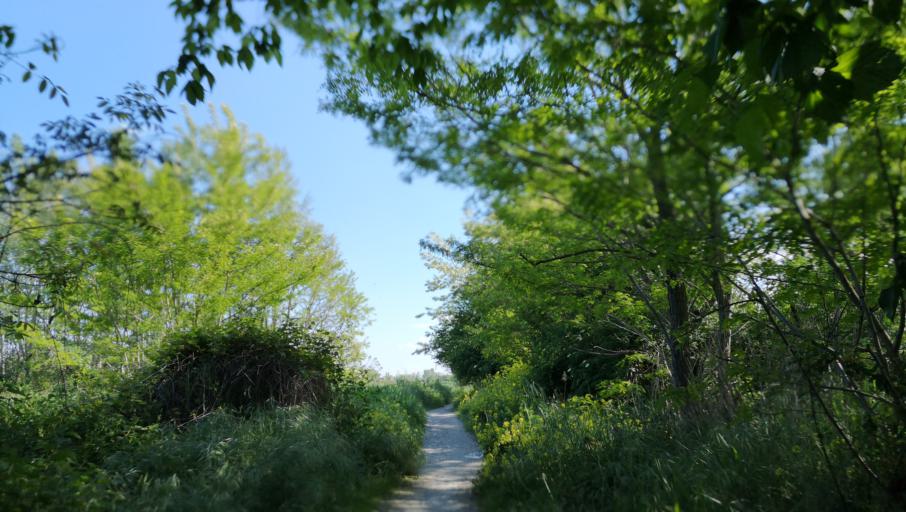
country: FR
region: Midi-Pyrenees
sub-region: Departement de la Haute-Garonne
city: Aucamville
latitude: 43.6617
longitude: 1.4066
